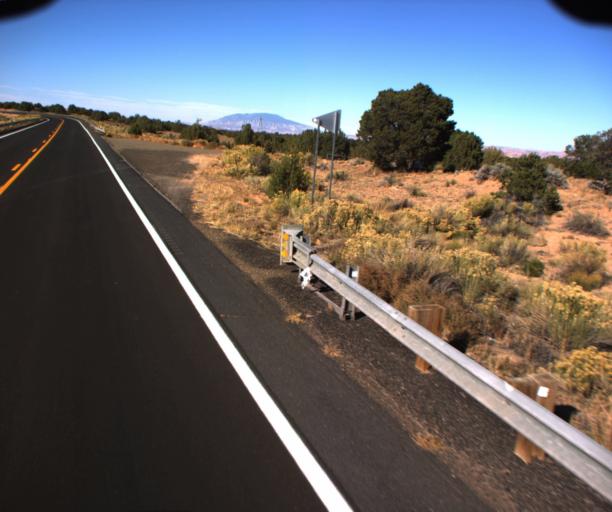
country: US
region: Arizona
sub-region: Coconino County
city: Kaibito
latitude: 36.6083
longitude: -110.9211
